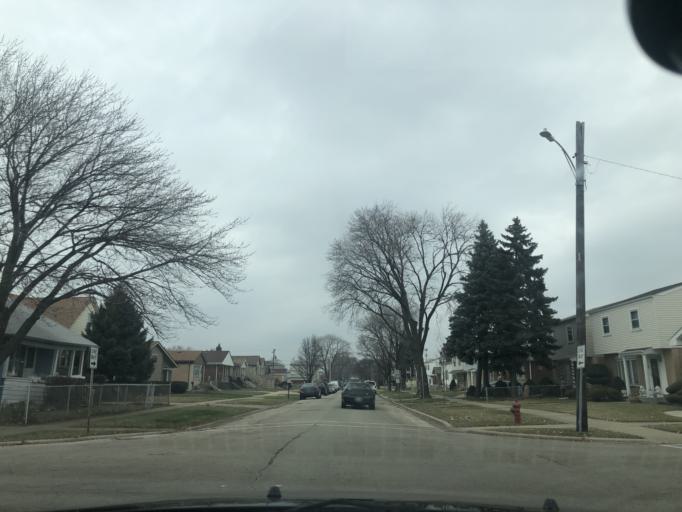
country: US
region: Illinois
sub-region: Cook County
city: Schiller Park
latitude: 41.9676
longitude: -87.8686
